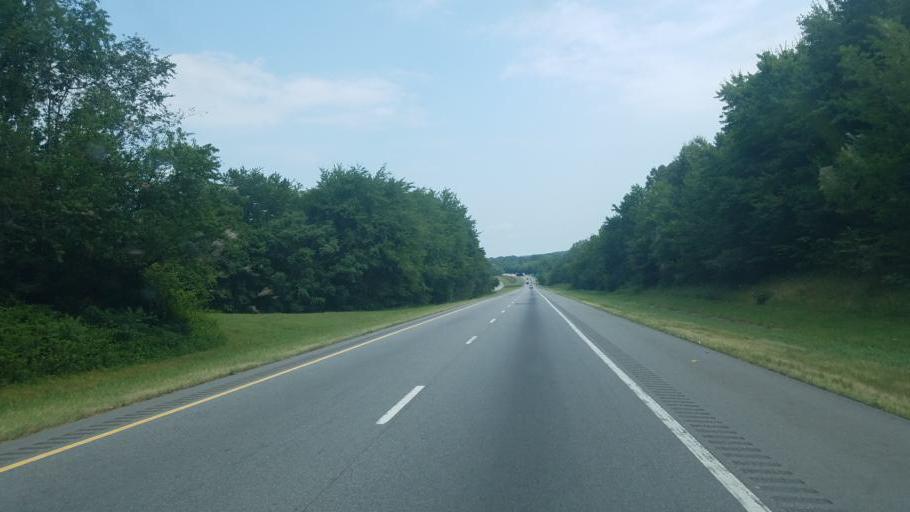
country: US
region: North Carolina
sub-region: Yadkin County
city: Jonesville
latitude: 36.0835
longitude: -80.8168
